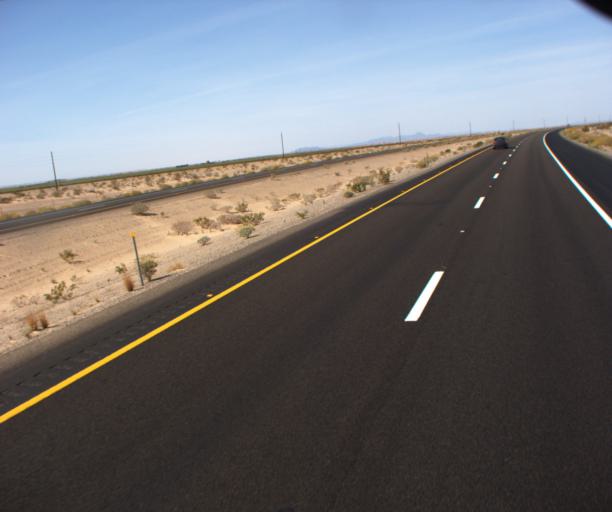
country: US
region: Arizona
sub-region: Yuma County
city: Somerton
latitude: 32.5130
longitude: -114.5603
